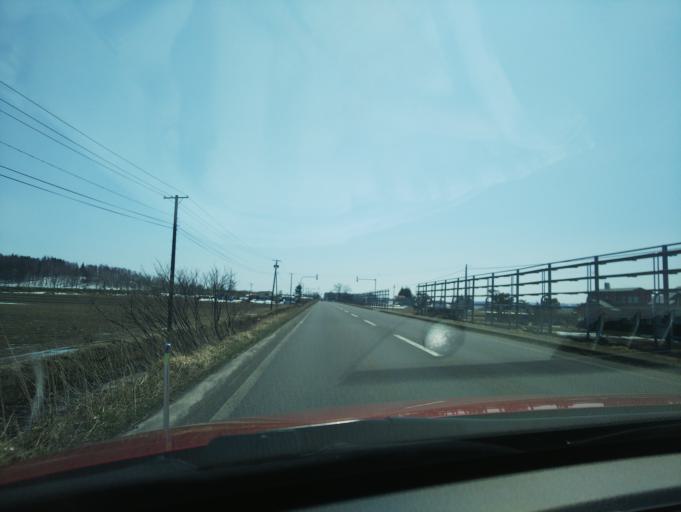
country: JP
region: Hokkaido
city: Nayoro
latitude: 44.2643
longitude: 142.3946
